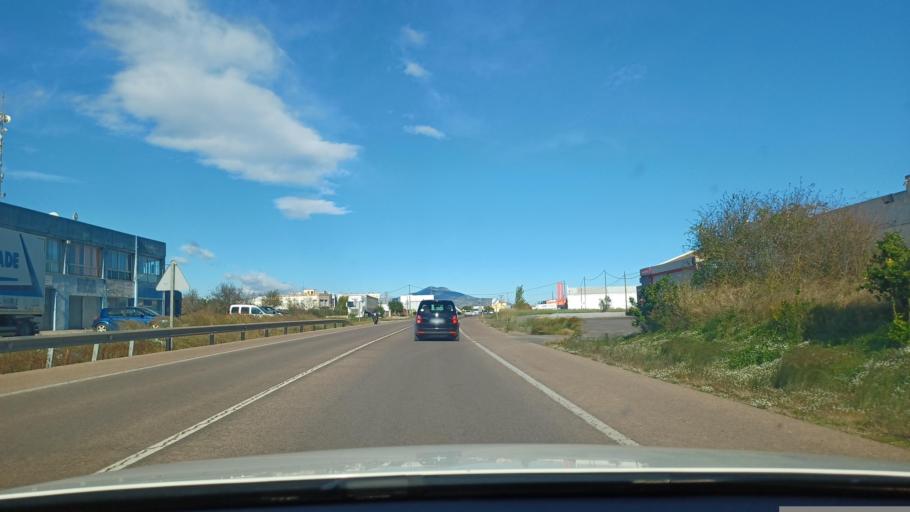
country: ES
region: Valencia
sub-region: Provincia de Castello
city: Vinaros
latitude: 40.4727
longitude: 0.4658
